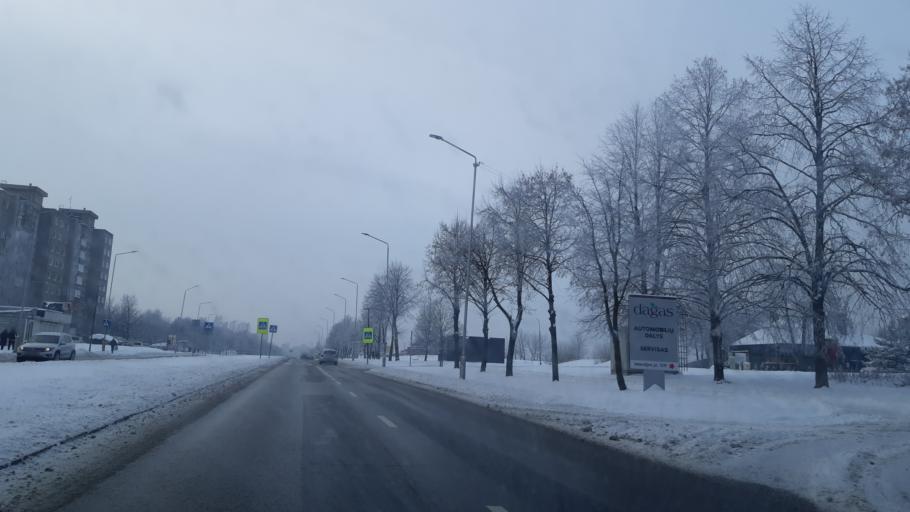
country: LT
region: Kauno apskritis
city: Dainava (Kaunas)
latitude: 54.9310
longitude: 23.9599
